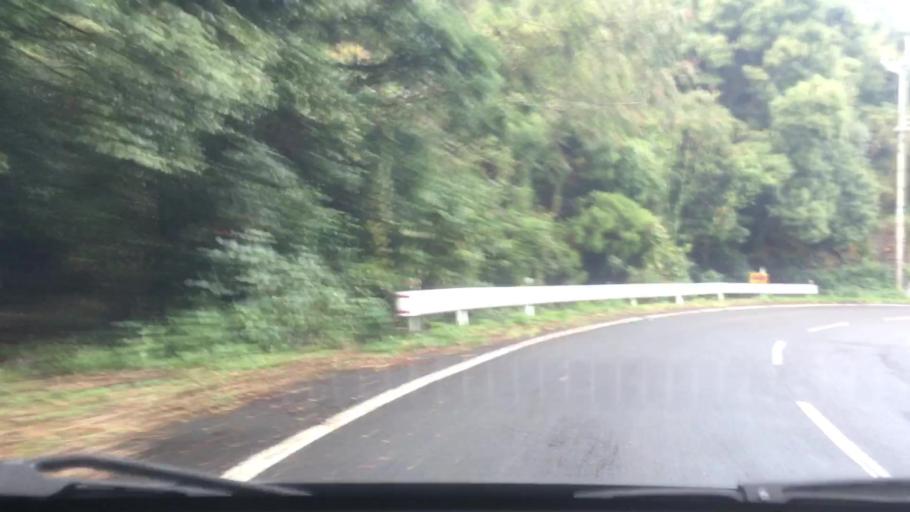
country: JP
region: Nagasaki
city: Sasebo
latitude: 32.9844
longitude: 129.7174
